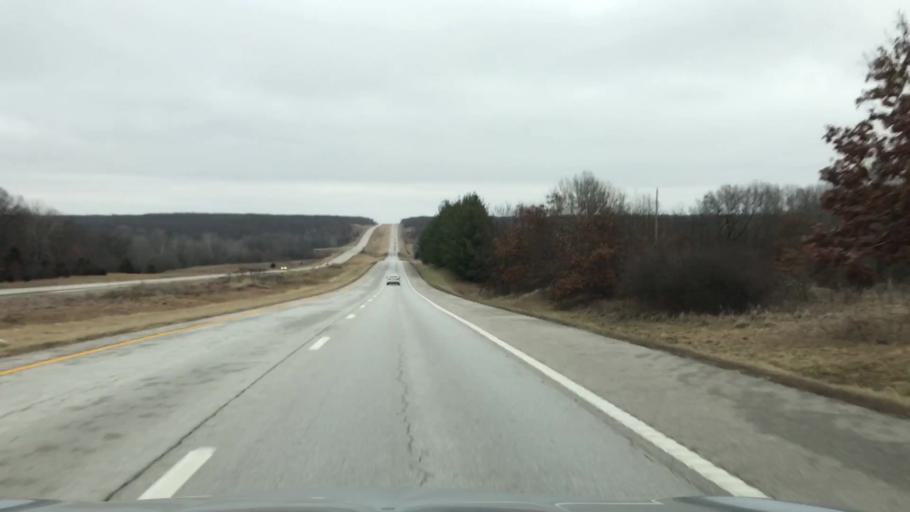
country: US
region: Missouri
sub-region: Linn County
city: Marceline
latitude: 39.7590
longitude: -92.8655
